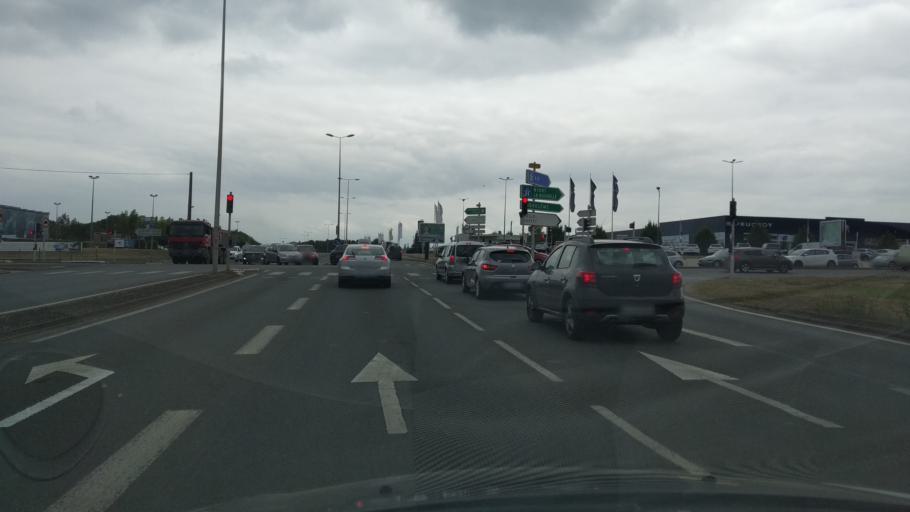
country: FR
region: Poitou-Charentes
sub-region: Departement de la Vienne
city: Biard
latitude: 46.5548
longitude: 0.3064
